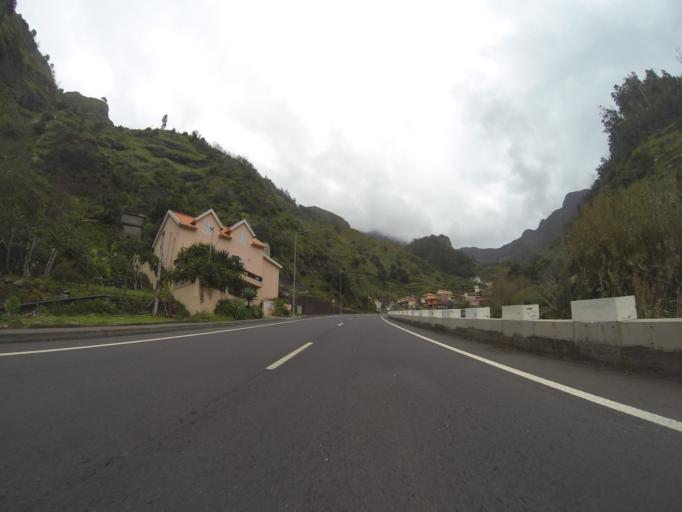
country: PT
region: Madeira
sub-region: Camara de Lobos
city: Curral das Freiras
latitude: 32.7340
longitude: -17.0211
